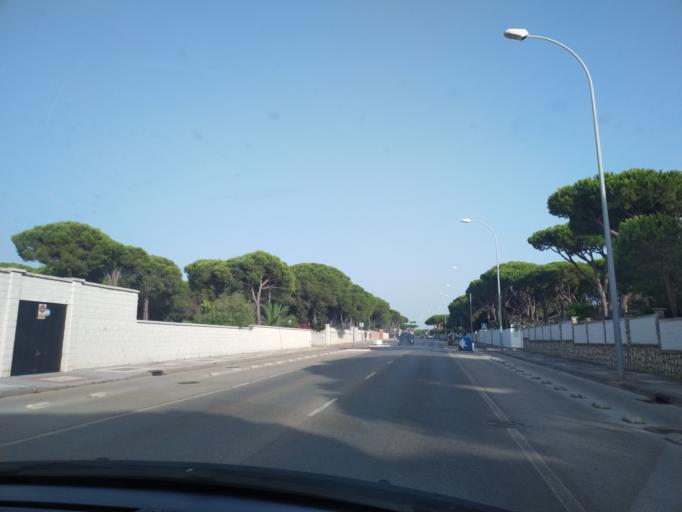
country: ES
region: Andalusia
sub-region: Provincia de Cadiz
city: Chiclana de la Frontera
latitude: 36.3790
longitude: -6.1900
